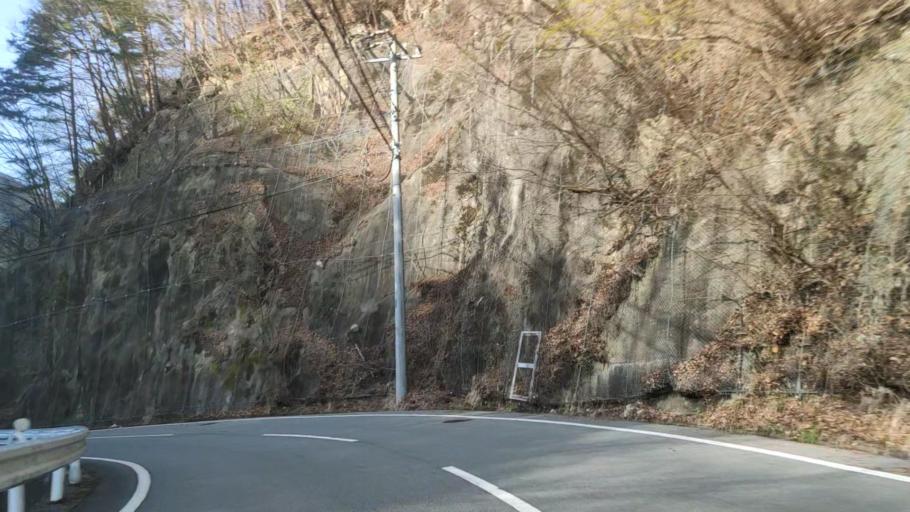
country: JP
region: Yamanashi
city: Fujikawaguchiko
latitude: 35.5526
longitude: 138.6619
